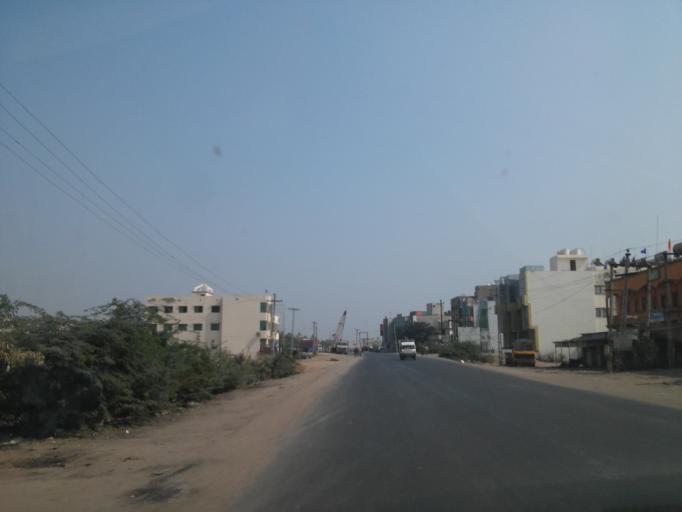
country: IN
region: Gujarat
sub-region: Kachchh
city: Mundra
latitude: 22.8383
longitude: 69.7030
